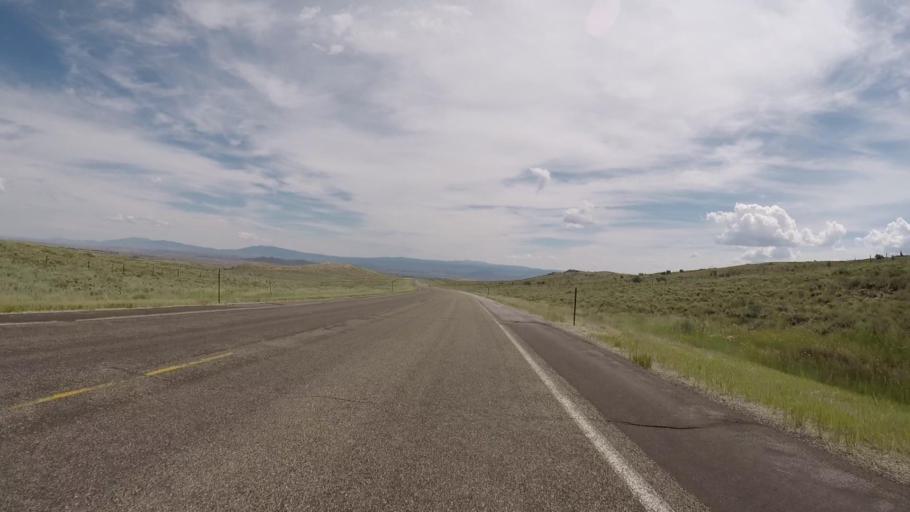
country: US
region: Wyoming
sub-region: Carbon County
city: Saratoga
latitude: 41.1972
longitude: -106.8417
